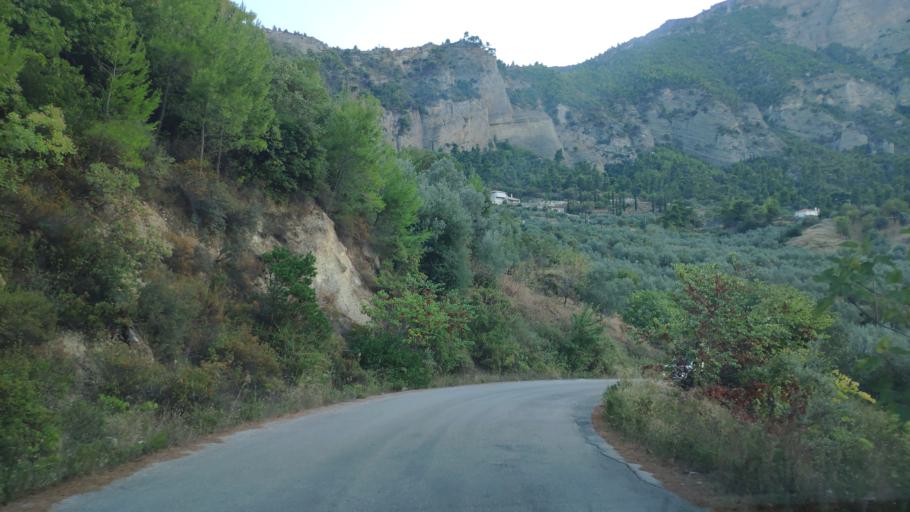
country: GR
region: West Greece
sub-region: Nomos Achaias
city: Aiyira
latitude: 38.0993
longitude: 22.4045
